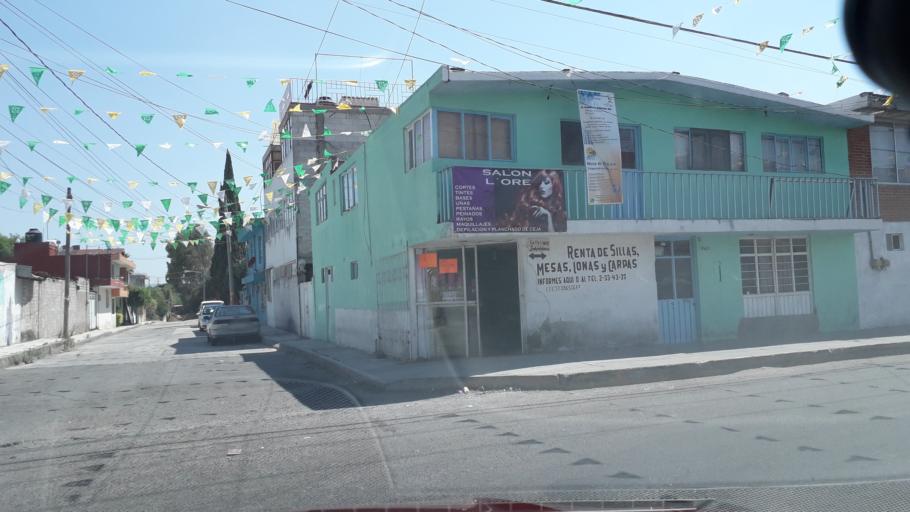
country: MX
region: Puebla
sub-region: Puebla
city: El Capulo (La Quebradora)
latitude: 18.9763
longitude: -98.2180
